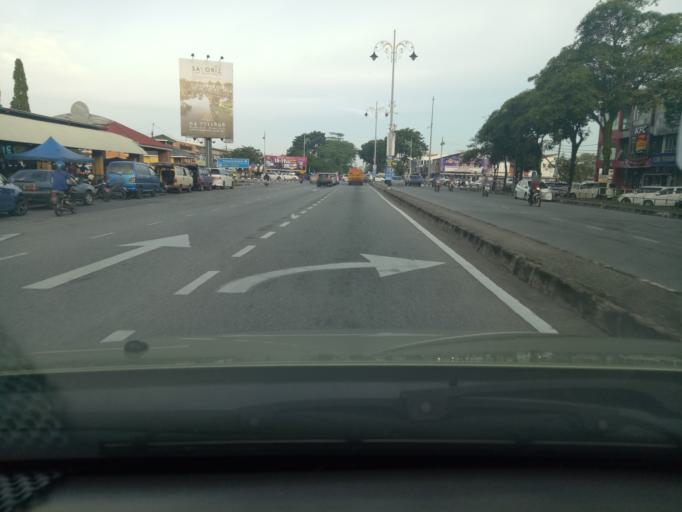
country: MY
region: Kedah
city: Alor Setar
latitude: 6.1255
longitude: 100.3567
